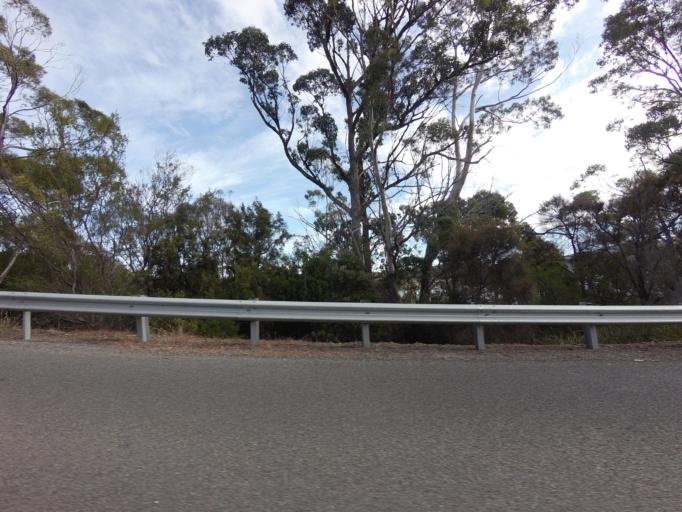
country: AU
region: Tasmania
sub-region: Clarence
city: Sandford
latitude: -43.1089
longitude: 147.7458
